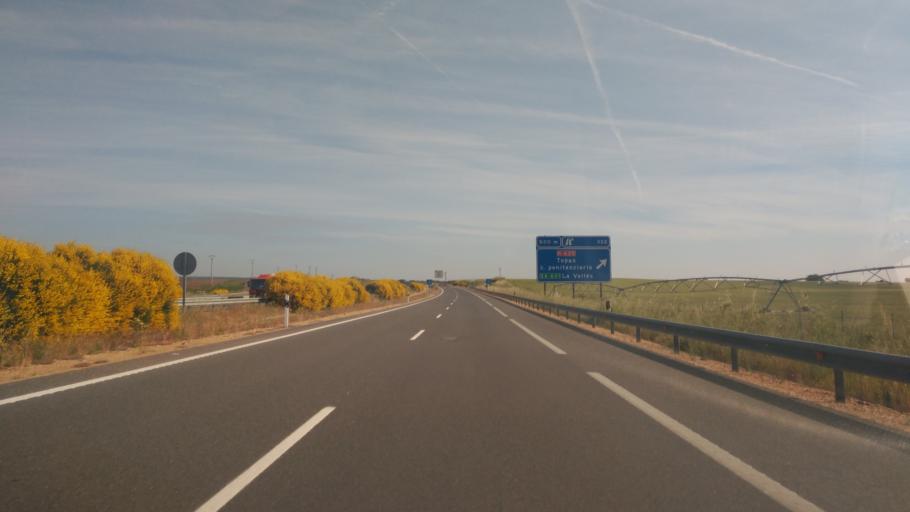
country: ES
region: Castille and Leon
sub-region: Provincia de Salamanca
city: Calzada de Valdunciel
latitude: 41.1125
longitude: -5.6986
